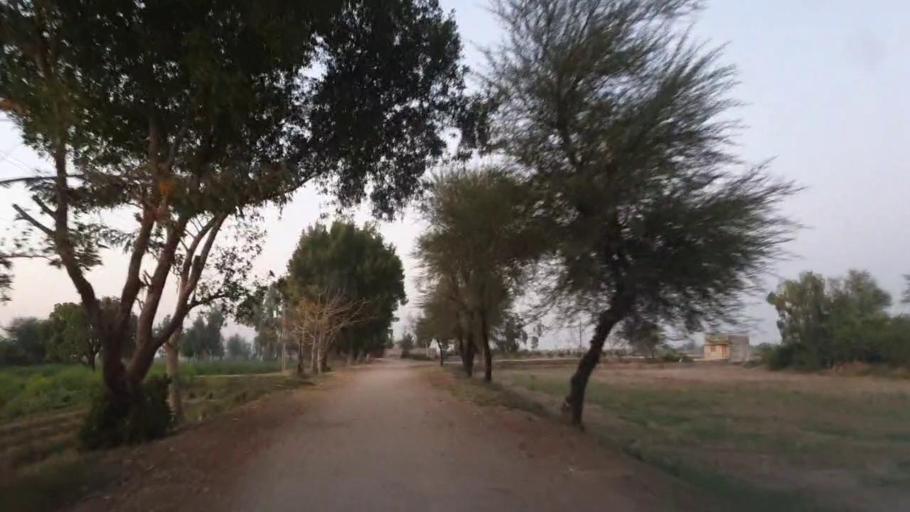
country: PK
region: Sindh
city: Samaro
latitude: 25.3441
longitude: 69.3979
